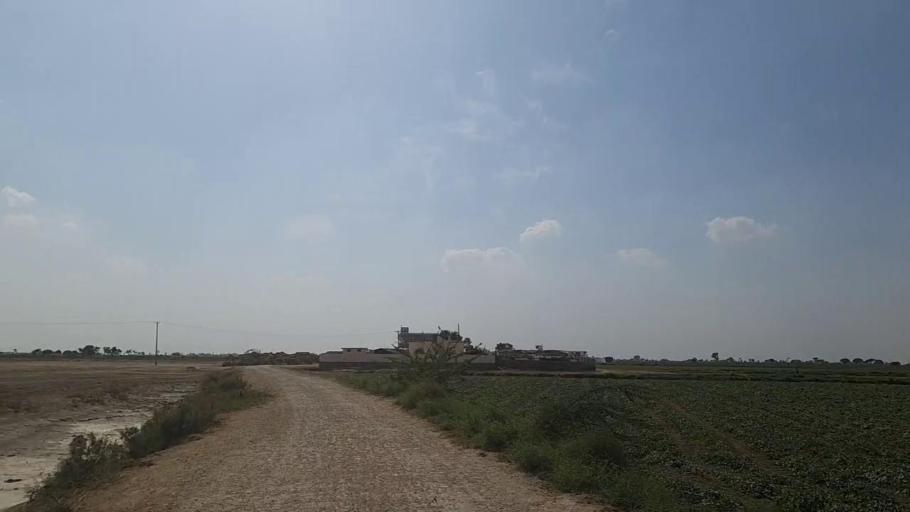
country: PK
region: Sindh
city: Jati
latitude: 24.4792
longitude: 68.2667
